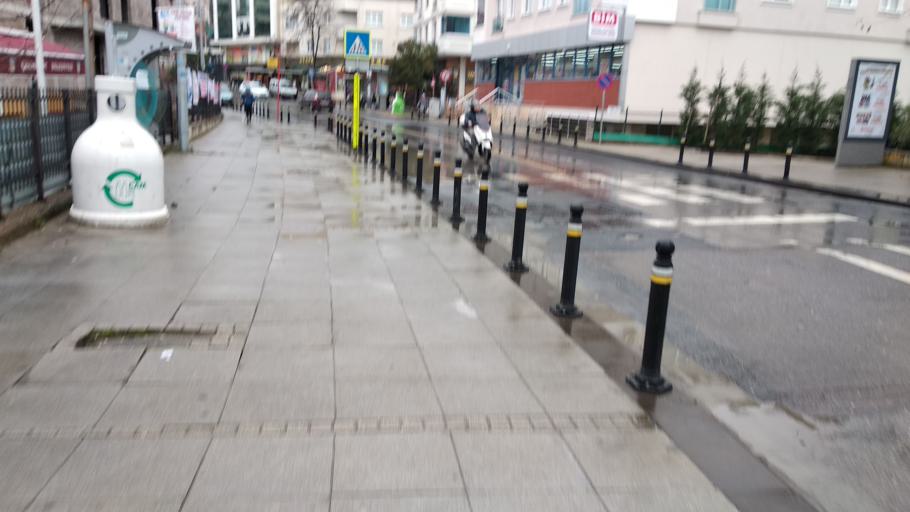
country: TR
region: Istanbul
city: Samandira
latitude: 41.0253
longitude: 29.1813
